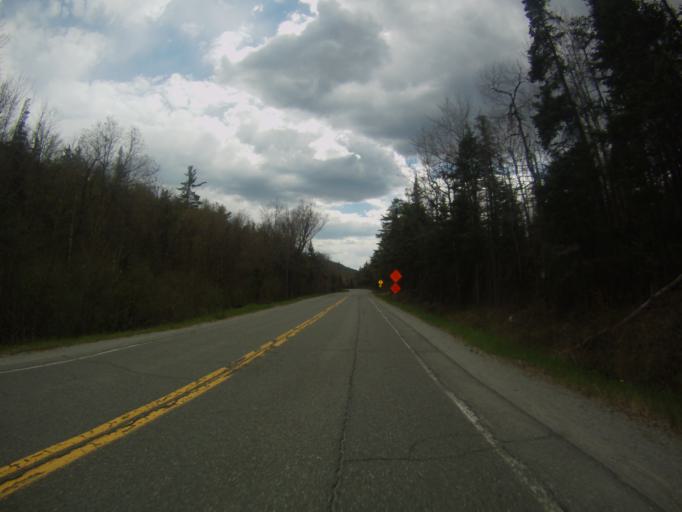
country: US
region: New York
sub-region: Essex County
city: Mineville
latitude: 44.0936
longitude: -73.5771
